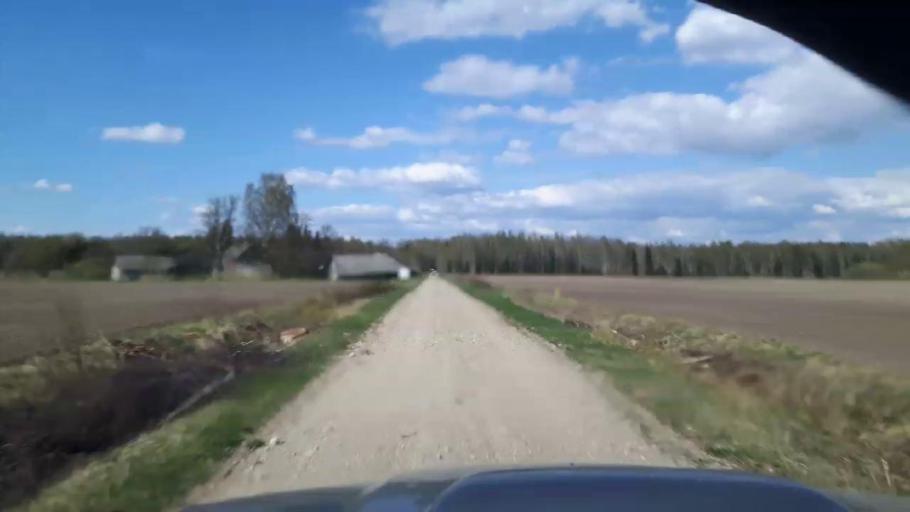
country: EE
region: Paernumaa
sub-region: Tootsi vald
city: Tootsi
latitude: 58.4532
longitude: 24.8453
